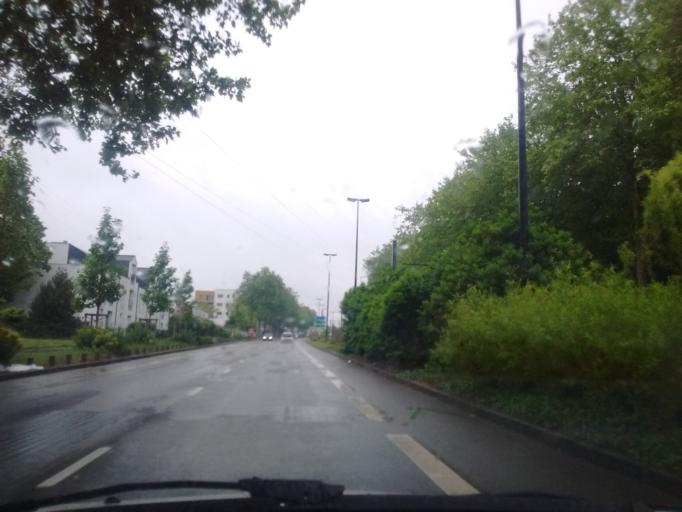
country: FR
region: Pays de la Loire
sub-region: Departement de la Loire-Atlantique
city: Sainte-Luce-sur-Loire
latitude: 47.2589
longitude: -1.5243
